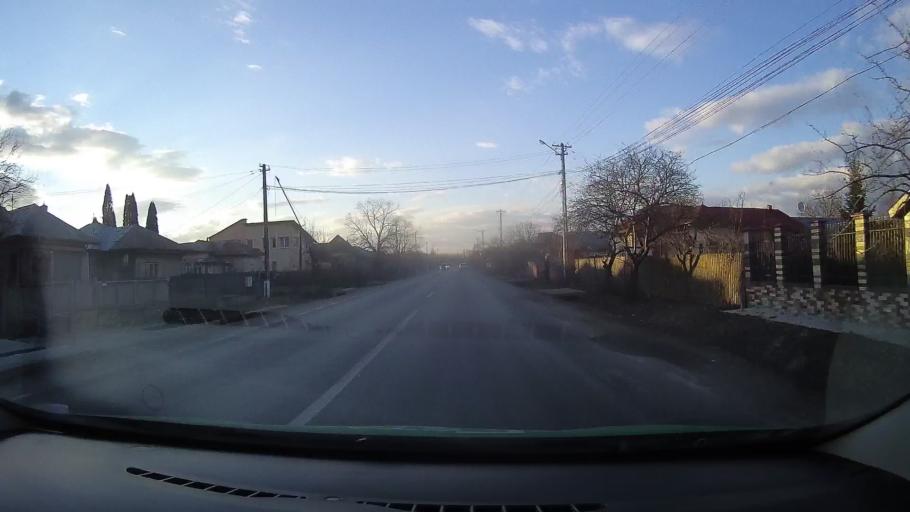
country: RO
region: Dambovita
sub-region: Comuna Gura Ocnitei
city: Adanca
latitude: 44.9086
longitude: 25.6196
